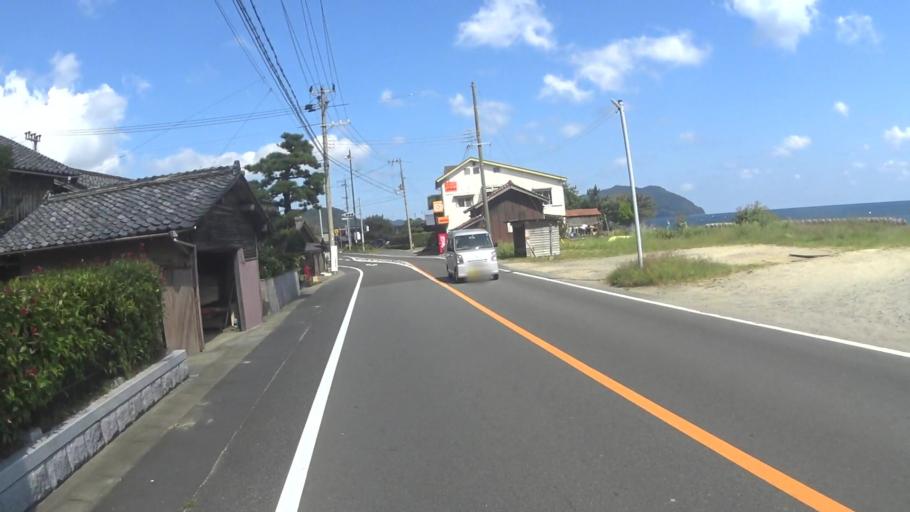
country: JP
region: Kyoto
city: Miyazu
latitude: 35.6553
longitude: 135.2582
